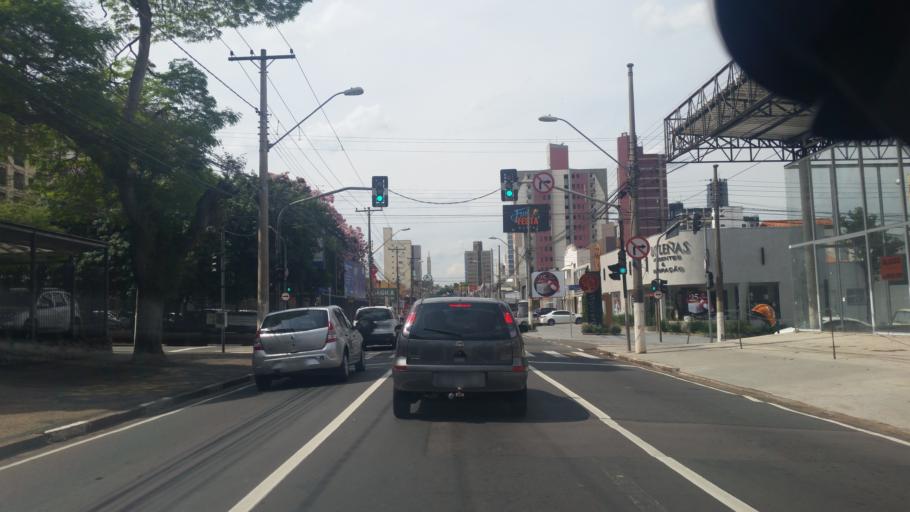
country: BR
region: Sao Paulo
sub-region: Campinas
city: Campinas
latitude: -22.8899
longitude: -47.0620
